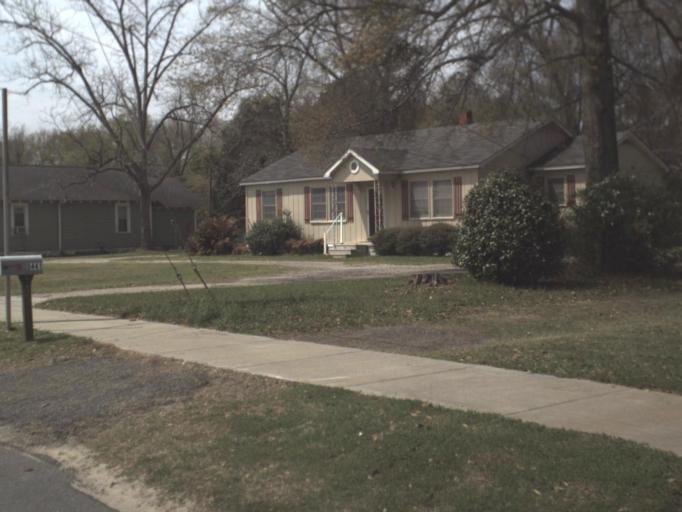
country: US
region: Florida
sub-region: Jackson County
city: Graceville
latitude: 30.9639
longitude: -85.5157
